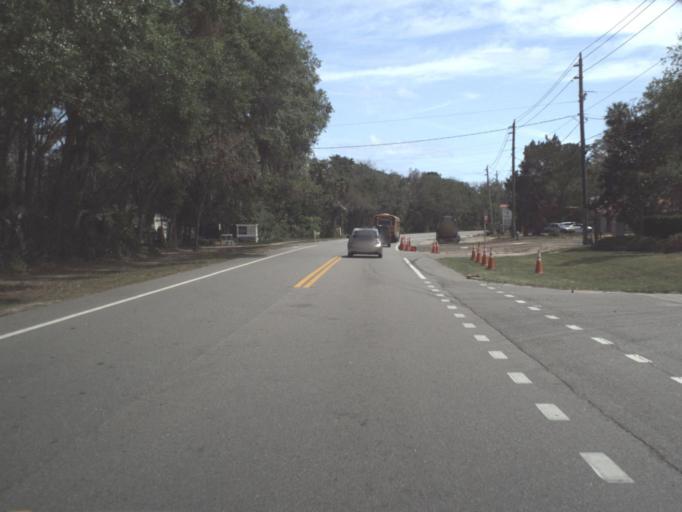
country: US
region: Florida
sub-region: Flagler County
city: Palm Coast
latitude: 29.5903
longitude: -81.1923
